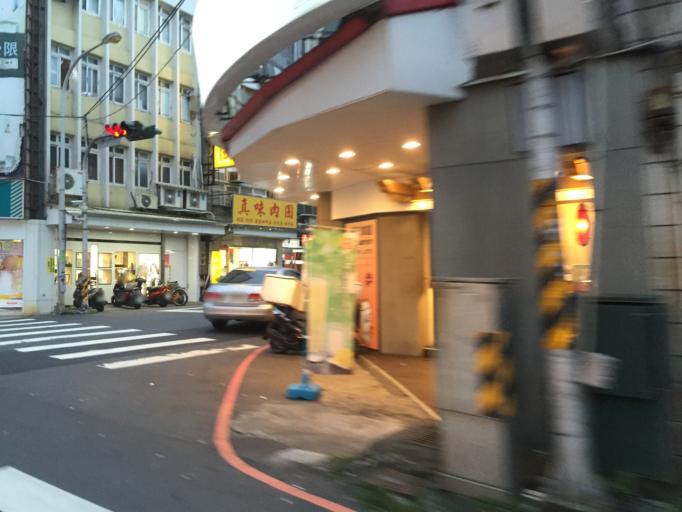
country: TW
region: Taiwan
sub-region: Yilan
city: Yilan
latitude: 24.7580
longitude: 121.7527
